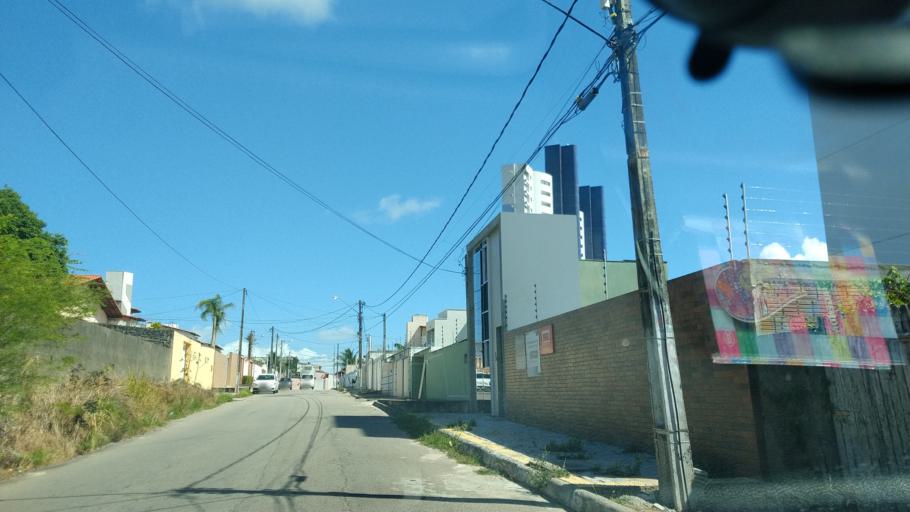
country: BR
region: Rio Grande do Norte
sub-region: Natal
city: Natal
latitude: -5.8707
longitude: -35.1912
